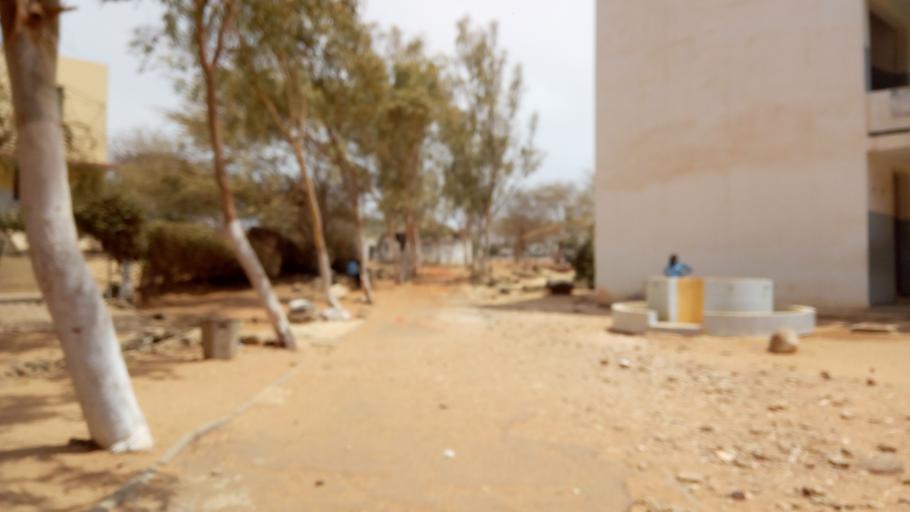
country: SN
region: Dakar
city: Grand Dakar
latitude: 14.7126
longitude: -17.4640
